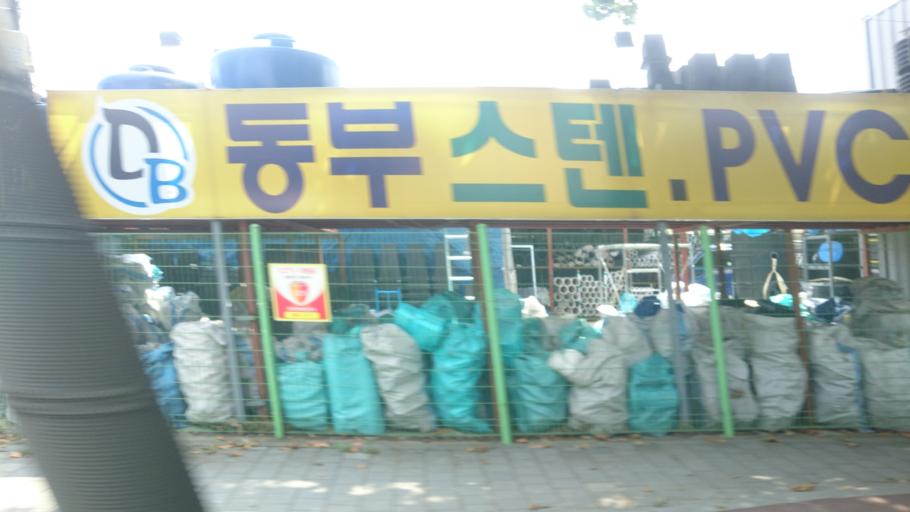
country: KR
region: Gyeongsangbuk-do
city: Gyeongsan-si
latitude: 35.8758
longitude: 128.6825
